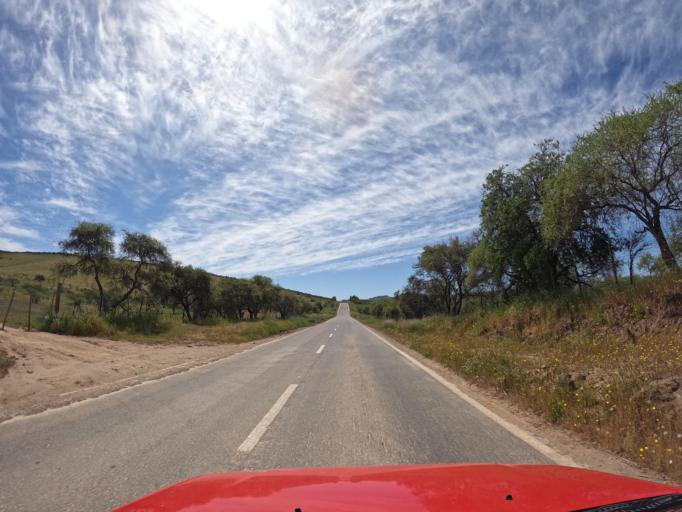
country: CL
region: Maule
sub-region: Provincia de Talca
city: Talca
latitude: -35.0201
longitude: -71.7716
